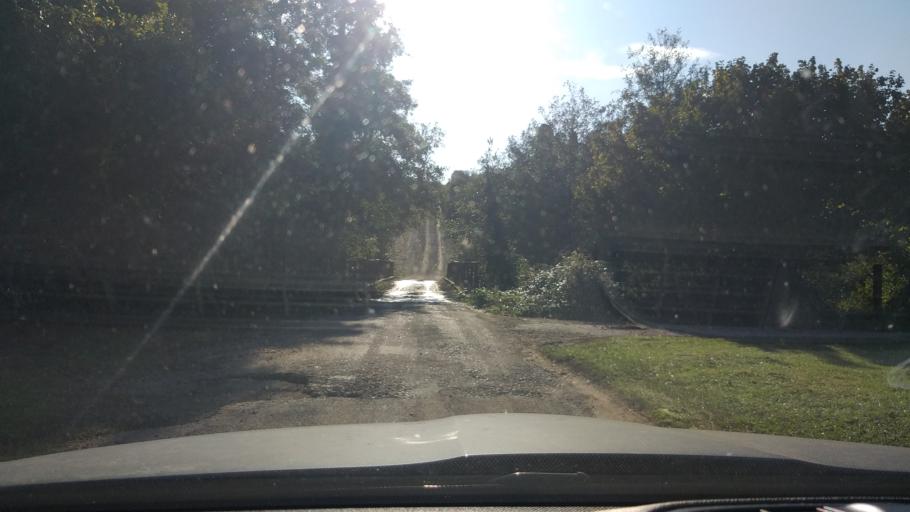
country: GE
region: Abkhazia
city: Stantsiya Novyy Afon
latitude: 43.0507
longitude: 40.8962
